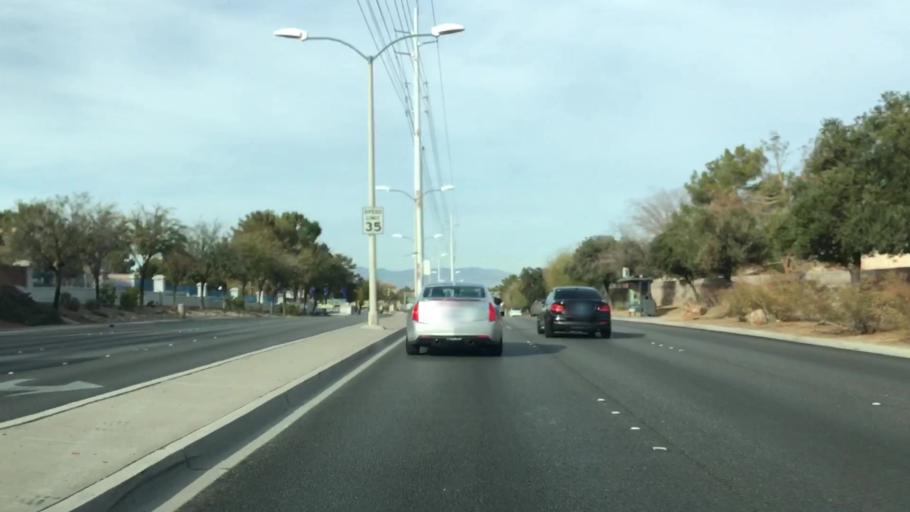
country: US
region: Nevada
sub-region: Clark County
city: Whitney
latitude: 36.0500
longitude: -115.0824
